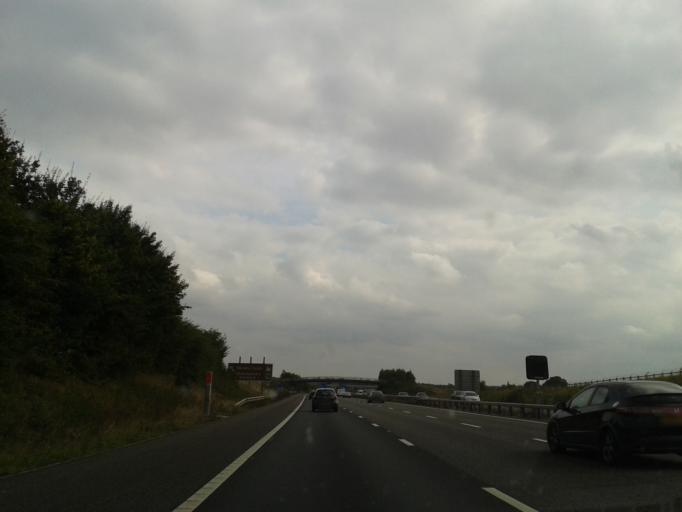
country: GB
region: England
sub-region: Warwickshire
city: Warwick
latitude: 52.2645
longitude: -1.6278
